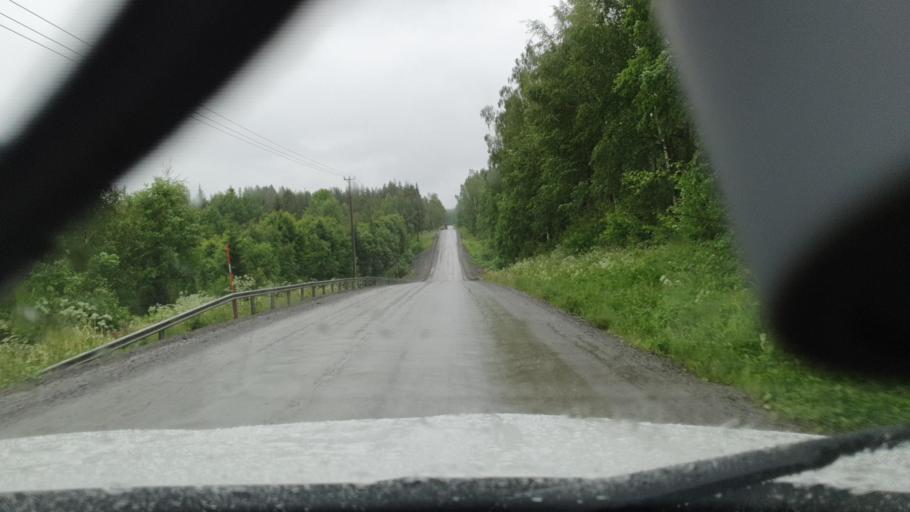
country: SE
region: Vaesterbotten
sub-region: Skelleftea Kommun
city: Burtraesk
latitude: 64.3552
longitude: 20.4768
